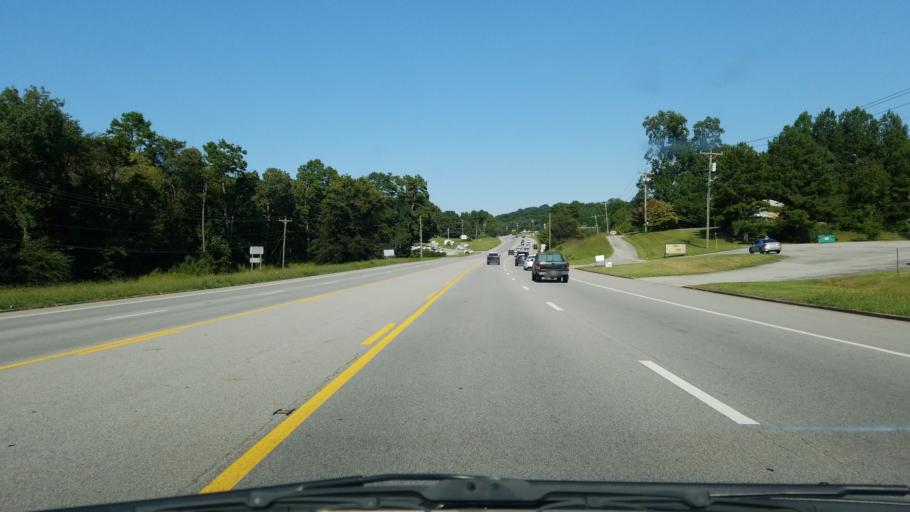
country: US
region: Tennessee
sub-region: Hamilton County
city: Harrison
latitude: 35.1117
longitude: -85.1371
